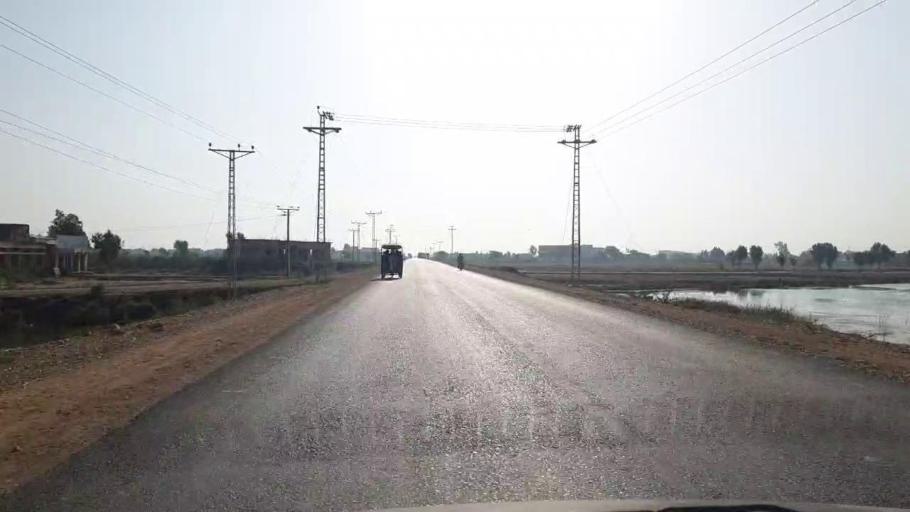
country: PK
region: Sindh
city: Badin
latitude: 24.6688
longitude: 68.8631
